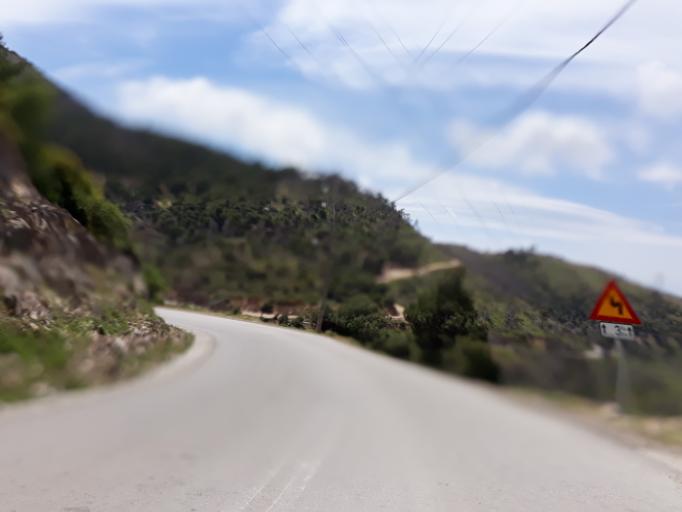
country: GR
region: Attica
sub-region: Nomarchia Dytikis Attikis
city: Magoula
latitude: 38.1692
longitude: 23.5471
